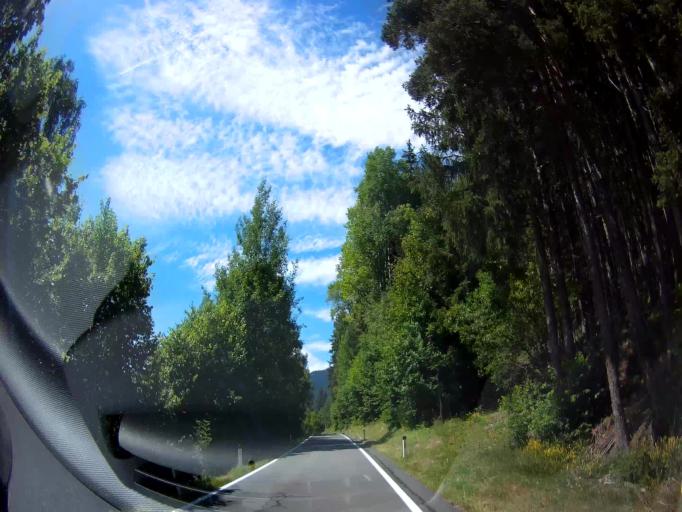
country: AT
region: Carinthia
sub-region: Politischer Bezirk Sankt Veit an der Glan
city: Glodnitz
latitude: 46.9073
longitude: 14.0969
